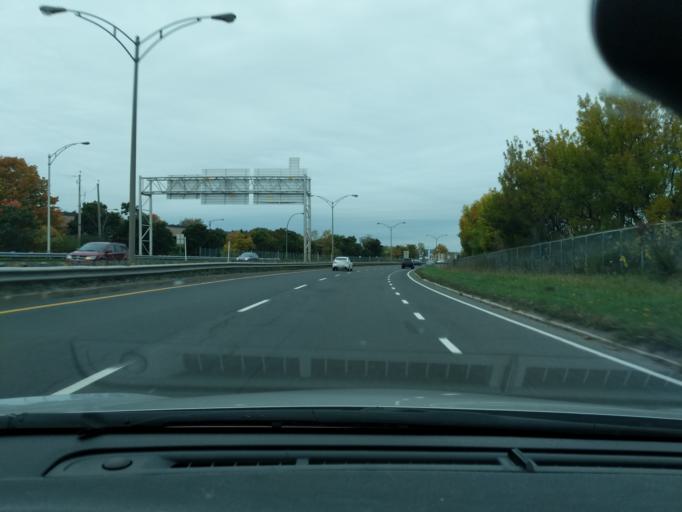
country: CA
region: Quebec
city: L'Ancienne-Lorette
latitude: 46.7620
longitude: -71.3077
